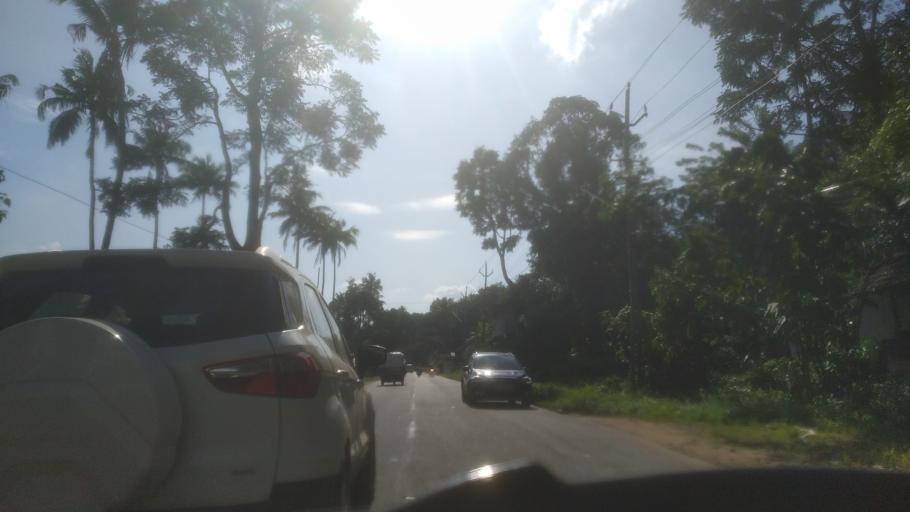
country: IN
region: Kerala
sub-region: Ernakulam
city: Muvattupuzha
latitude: 9.9843
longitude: 76.5615
